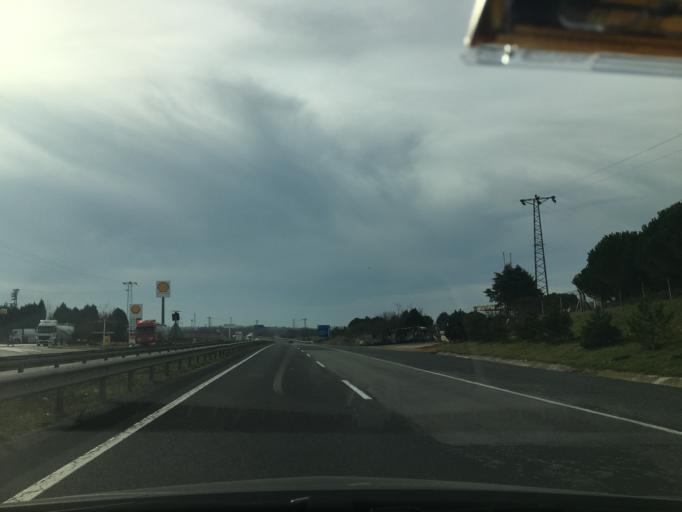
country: TR
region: Istanbul
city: Buyukcavuslu
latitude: 41.2046
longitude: 28.0758
